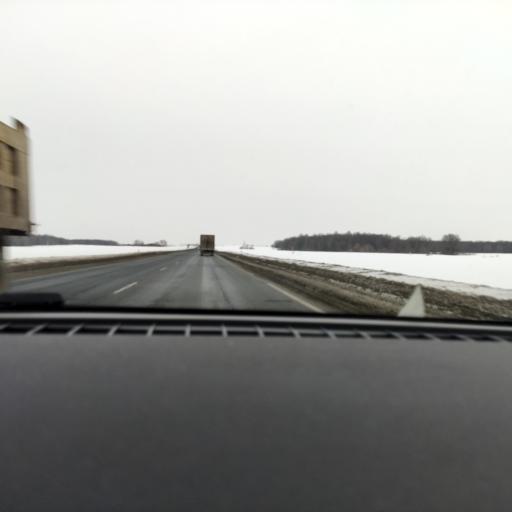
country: RU
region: Samara
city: Petra-Dubrava
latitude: 53.3245
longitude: 50.4549
